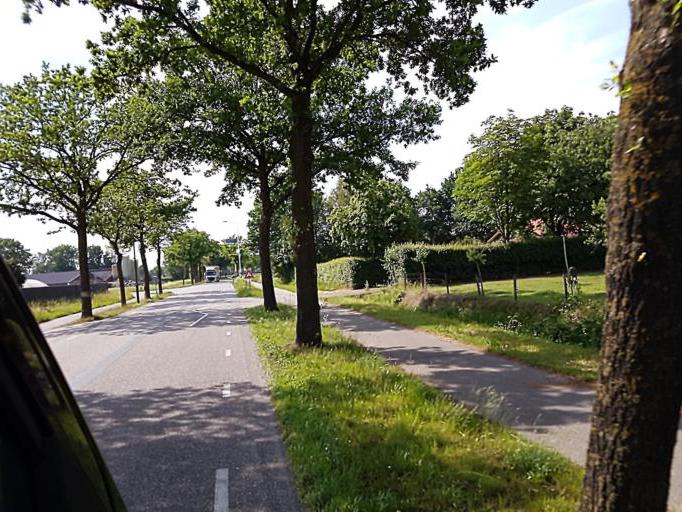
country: NL
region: North Brabant
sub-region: Gemeente Cranendonck
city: Cranendonck
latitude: 51.2639
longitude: 5.5947
